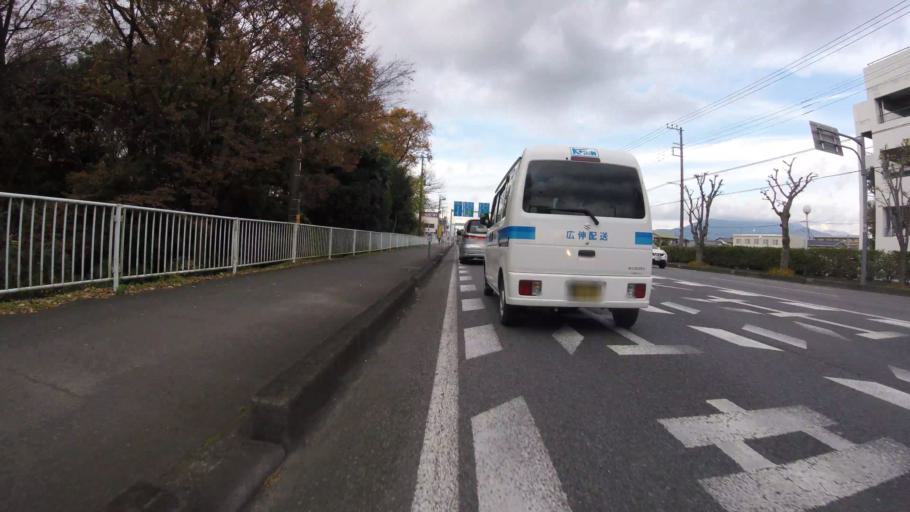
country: JP
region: Shizuoka
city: Mishima
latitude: 35.1082
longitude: 138.8999
